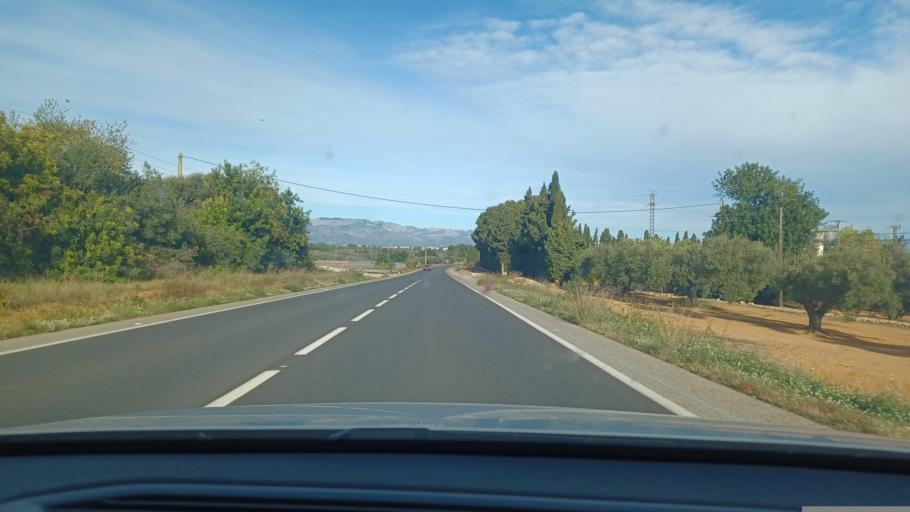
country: ES
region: Catalonia
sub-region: Provincia de Tarragona
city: Santa Barbara
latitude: 40.6855
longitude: 0.5091
